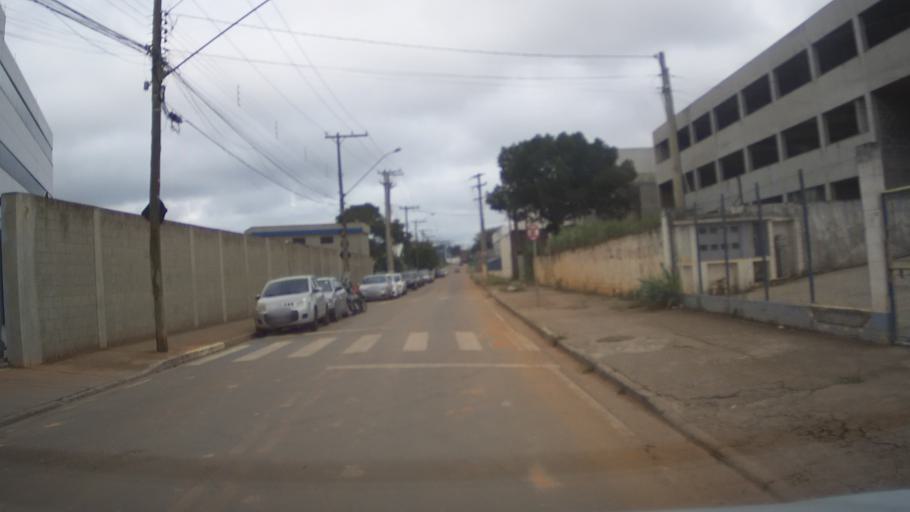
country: BR
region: Sao Paulo
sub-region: Aruja
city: Aruja
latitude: -23.4088
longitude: -46.3623
